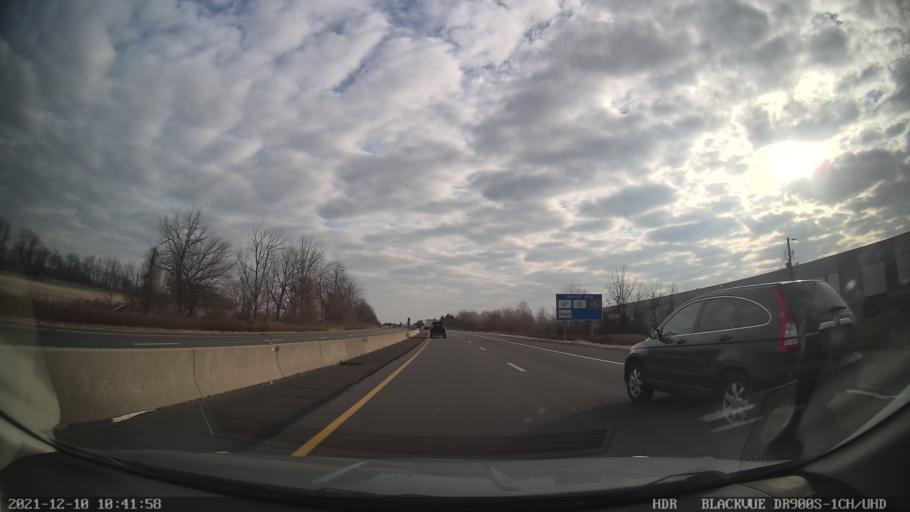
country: US
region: Pennsylvania
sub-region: Lehigh County
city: Breinigsville
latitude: 40.5747
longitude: -75.6549
